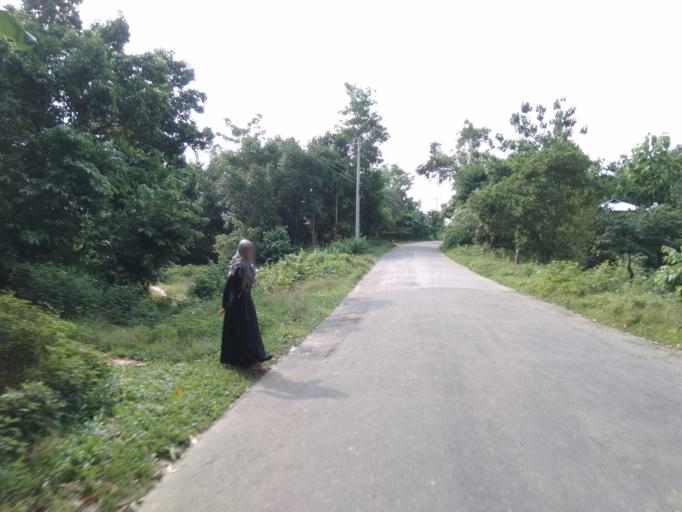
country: BD
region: Chittagong
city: Khagrachhari
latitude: 23.0325
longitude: 92.0094
